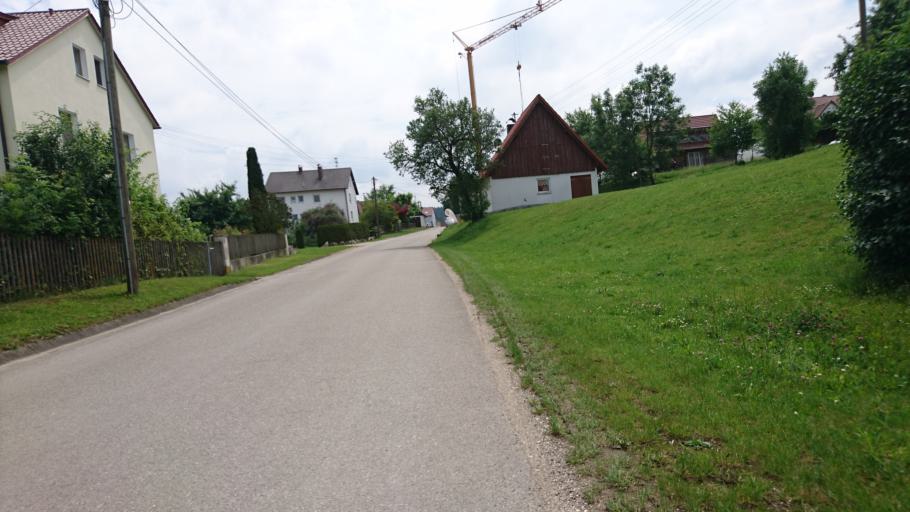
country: DE
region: Bavaria
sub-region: Swabia
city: Landensberg
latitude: 48.4361
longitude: 10.5039
